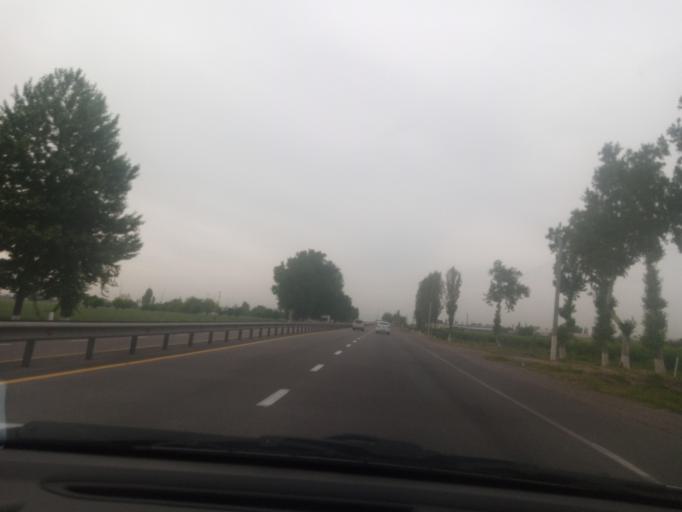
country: UZ
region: Toshkent Shahri
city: Bektemir
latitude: 41.1411
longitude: 69.4329
